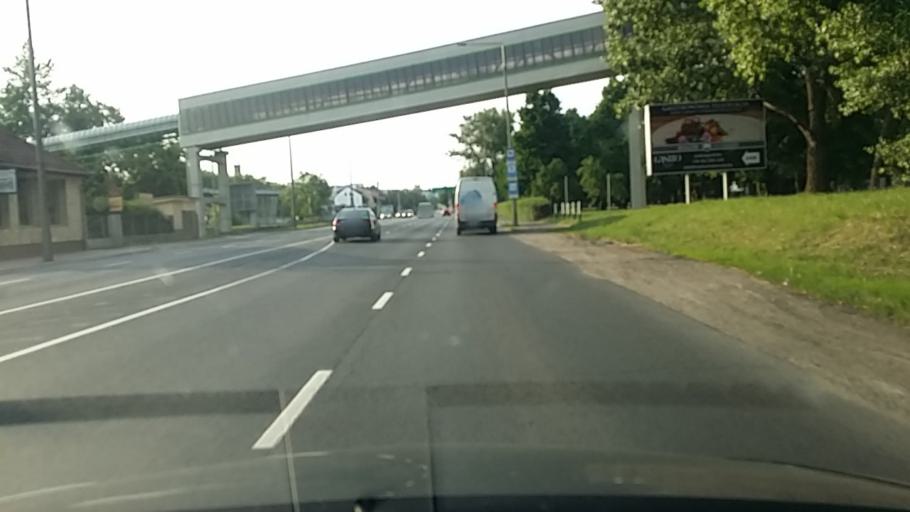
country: HU
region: Borsod-Abauj-Zemplen
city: Miskolc
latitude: 48.0651
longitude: 20.7932
